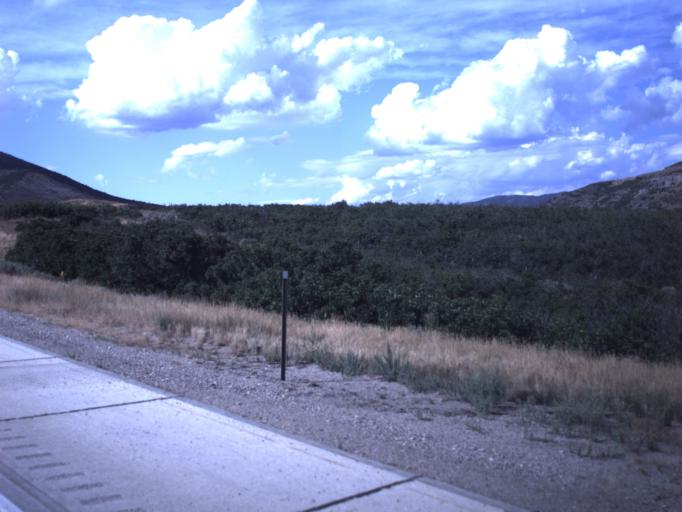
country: US
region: Utah
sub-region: Wasatch County
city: Heber
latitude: 40.5757
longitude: -111.4345
